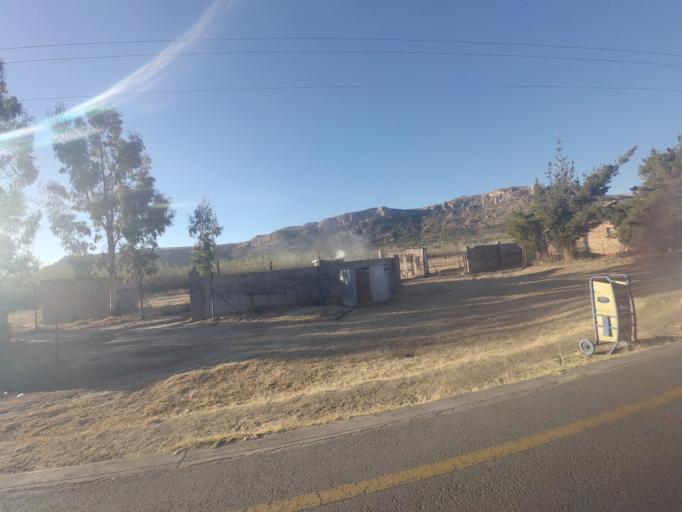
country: LS
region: Maseru
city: Maseru
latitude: -29.3525
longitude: 27.5448
